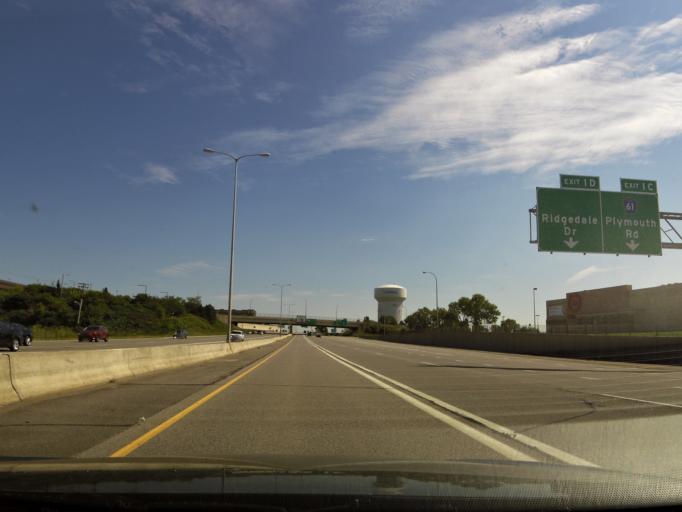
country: US
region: Minnesota
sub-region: Hennepin County
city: Minnetonka Mills
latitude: 44.9710
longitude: -93.4490
